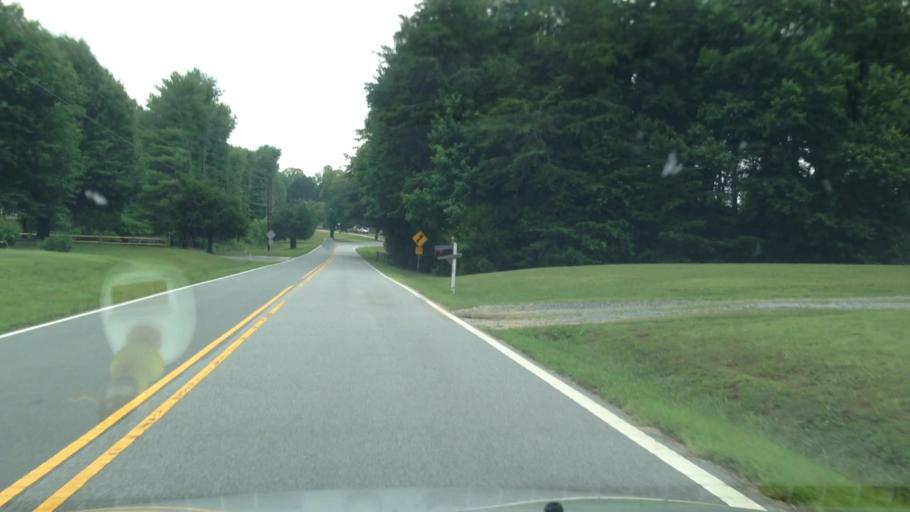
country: US
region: North Carolina
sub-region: Forsyth County
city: Kernersville
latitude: 36.1521
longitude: -80.0919
